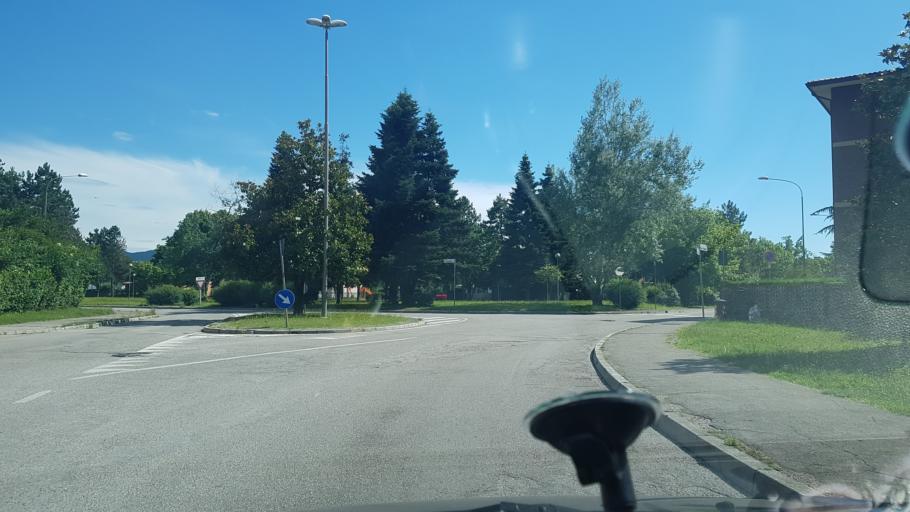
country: IT
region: Friuli Venezia Giulia
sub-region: Provincia di Gorizia
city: Gorizia
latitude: 45.9308
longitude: 13.6218
